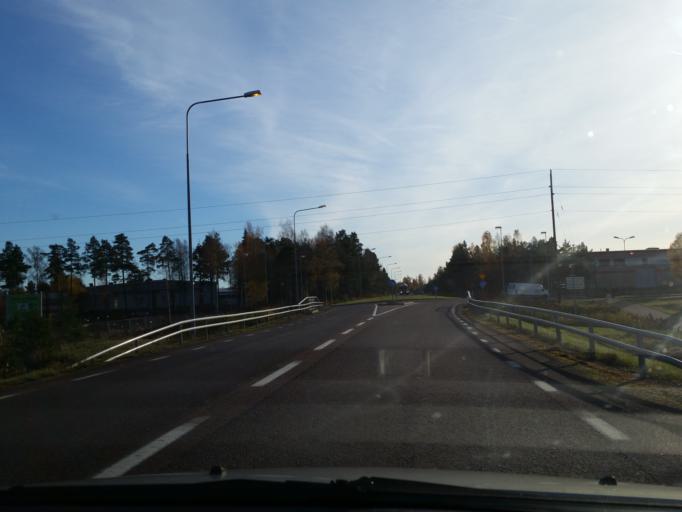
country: AX
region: Alands landsbygd
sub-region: Jomala
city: Jomala
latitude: 60.1290
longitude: 19.9345
